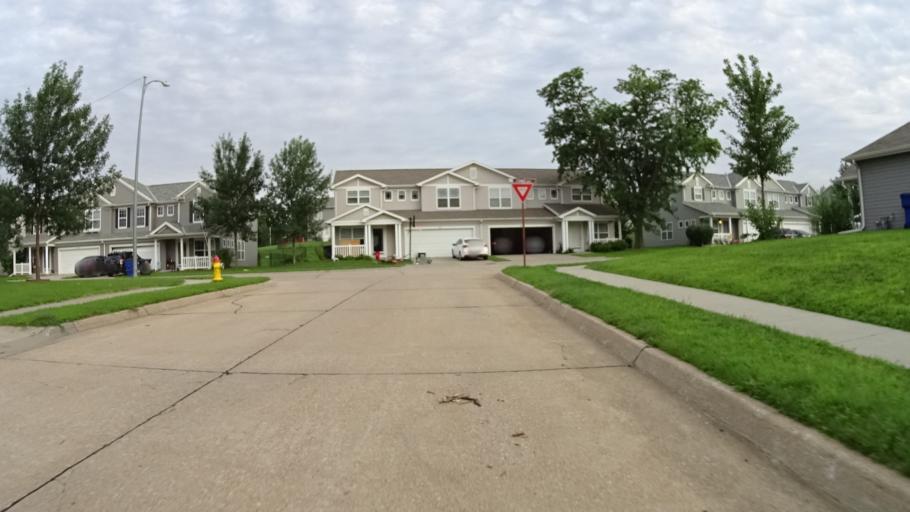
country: US
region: Nebraska
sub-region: Sarpy County
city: Offutt Air Force Base
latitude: 41.1237
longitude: -95.9489
